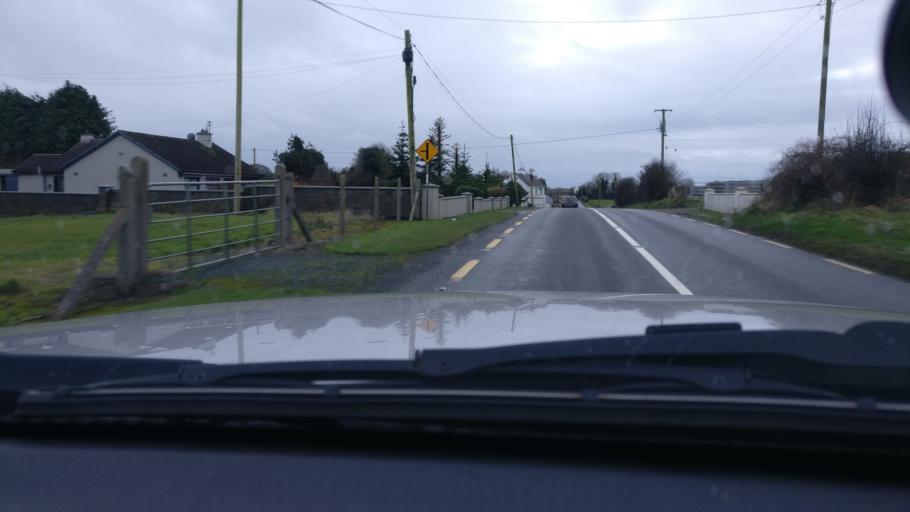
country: IE
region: Leinster
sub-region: An Longfort
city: Ballymahon
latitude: 53.5149
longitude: -7.8223
